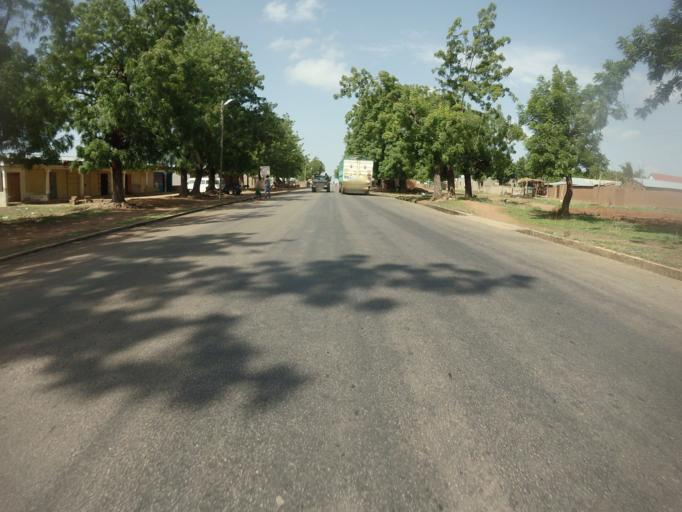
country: GH
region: Upper East
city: Bawku
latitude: 11.0690
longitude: -0.2090
